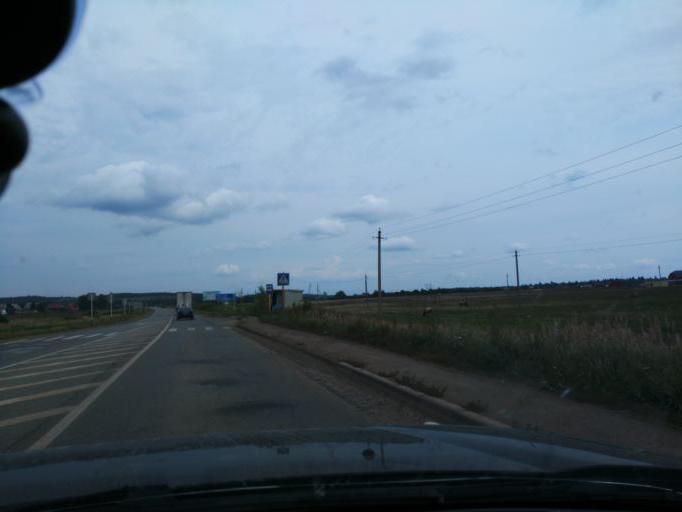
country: RU
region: Perm
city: Kuyeda
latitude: 56.4494
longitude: 55.6033
